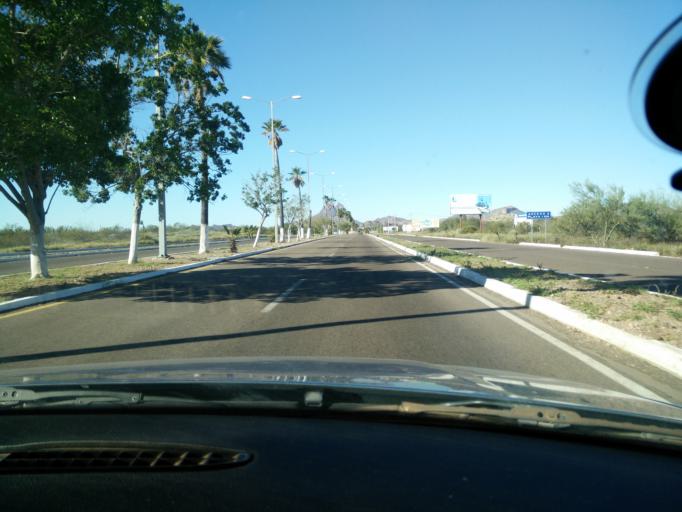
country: MX
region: Sonora
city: Heroica Guaymas
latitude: 27.9695
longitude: -111.0029
